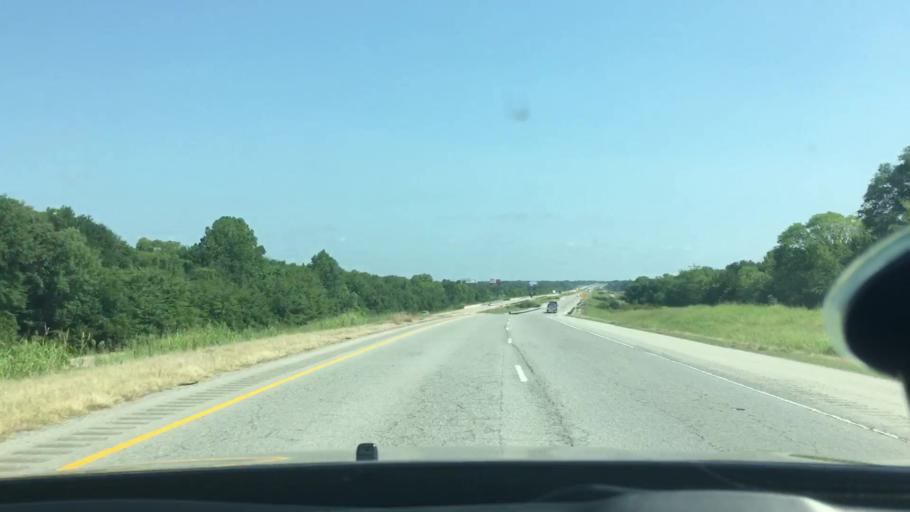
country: US
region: Oklahoma
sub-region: Atoka County
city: Atoka
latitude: 34.2378
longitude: -96.2204
